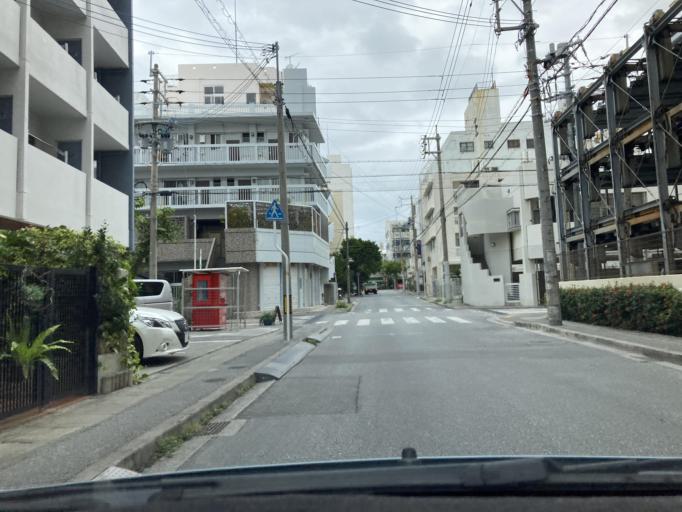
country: JP
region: Okinawa
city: Naha-shi
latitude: 26.2132
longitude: 127.6731
